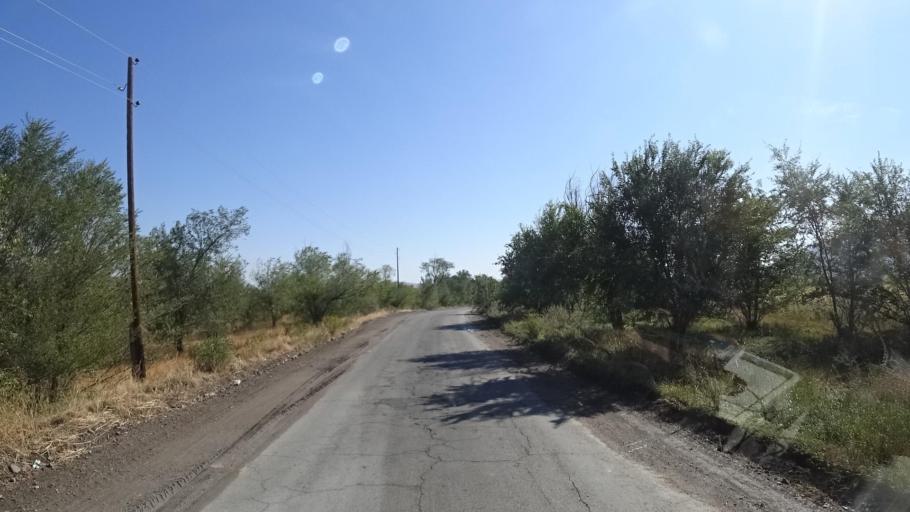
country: KG
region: Chuy
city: Bishkek
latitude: 42.7352
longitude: 74.5216
